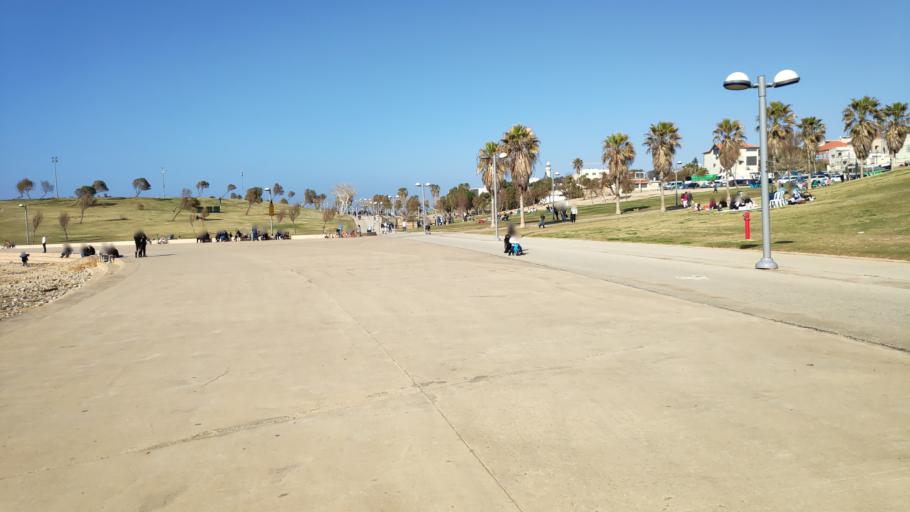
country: IL
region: Tel Aviv
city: Yafo
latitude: 32.0437
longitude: 34.7464
